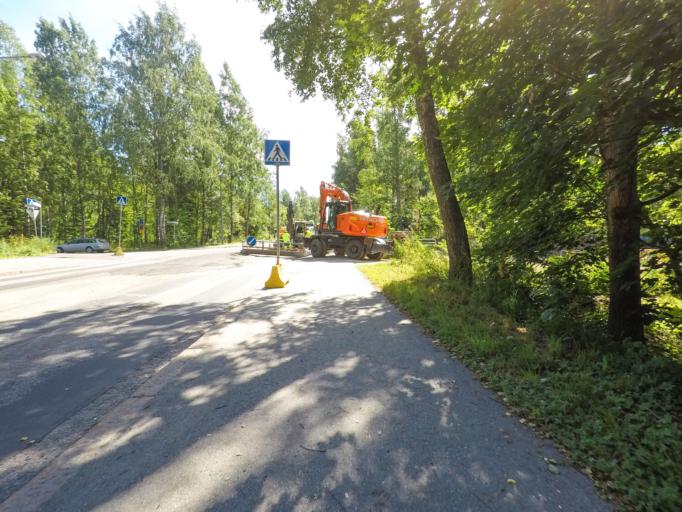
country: FI
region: Uusimaa
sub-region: Helsinki
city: Vantaa
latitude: 60.2060
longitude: 25.0575
